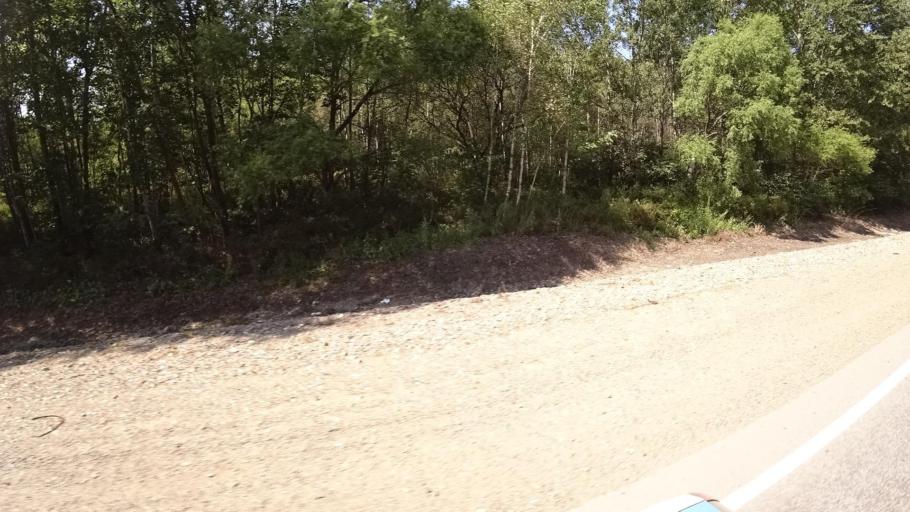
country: RU
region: Khabarovsk Krai
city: Khor
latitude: 47.9848
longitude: 135.0889
